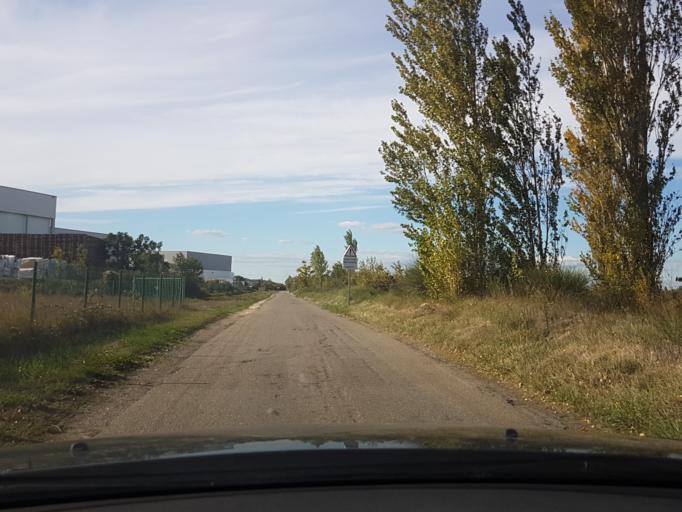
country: FR
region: Provence-Alpes-Cote d'Azur
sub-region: Departement du Vaucluse
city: Entraigues-sur-la-Sorgue
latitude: 43.9838
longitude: 4.9360
